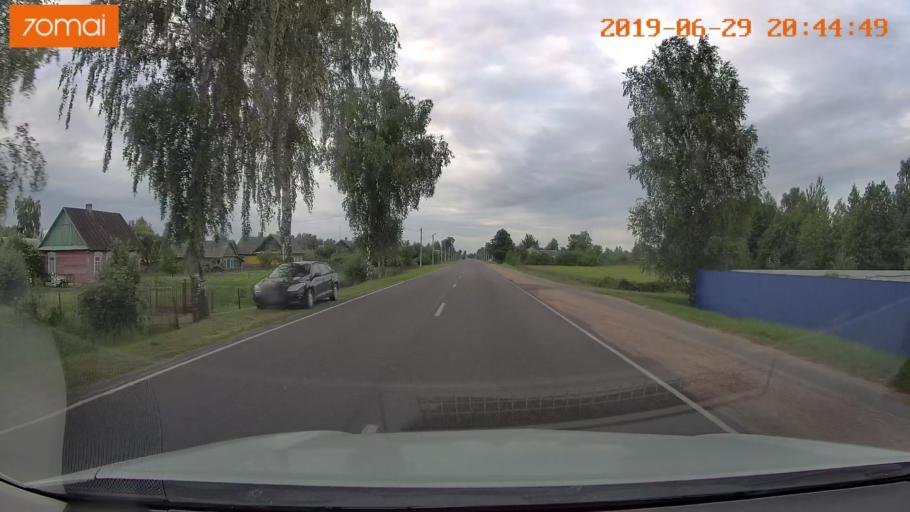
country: BY
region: Brest
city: Hantsavichy
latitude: 52.6174
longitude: 26.3074
